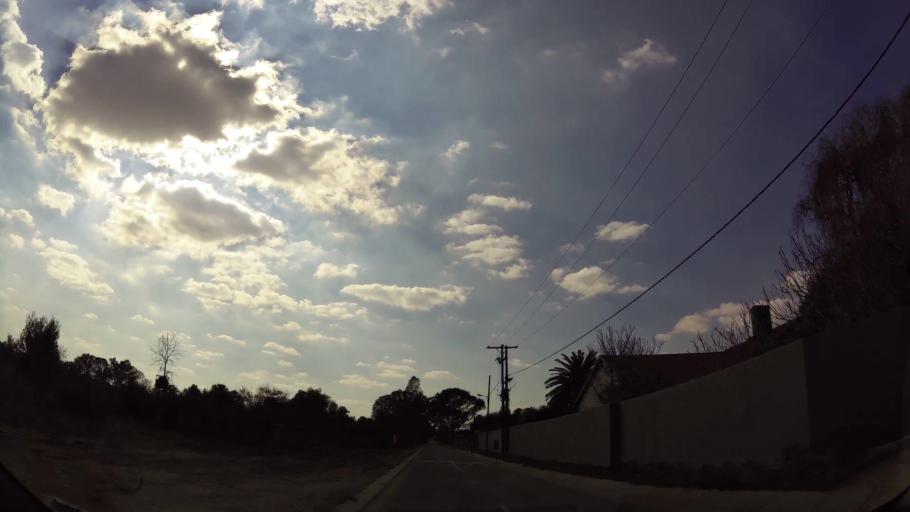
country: ZA
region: Gauteng
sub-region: Ekurhuleni Metropolitan Municipality
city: Benoni
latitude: -26.1040
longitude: 28.3603
